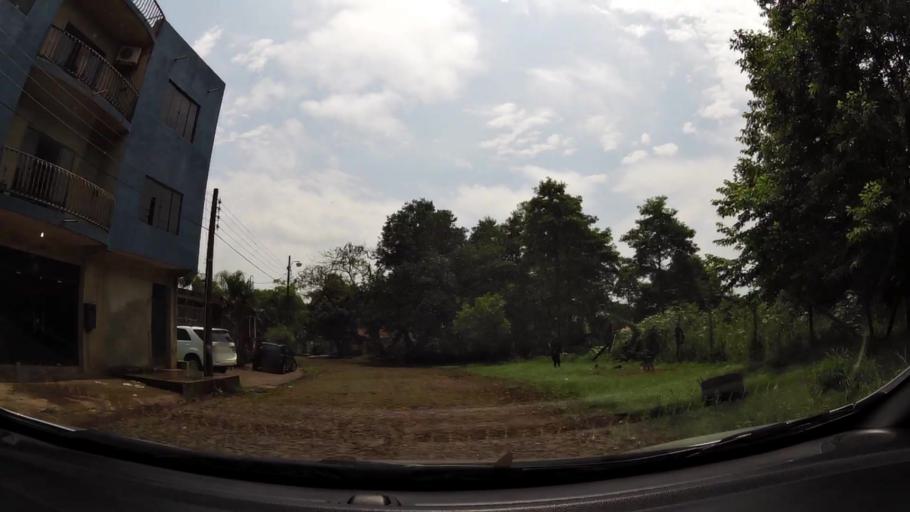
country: PY
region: Alto Parana
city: Ciudad del Este
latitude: -25.5024
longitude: -54.6605
